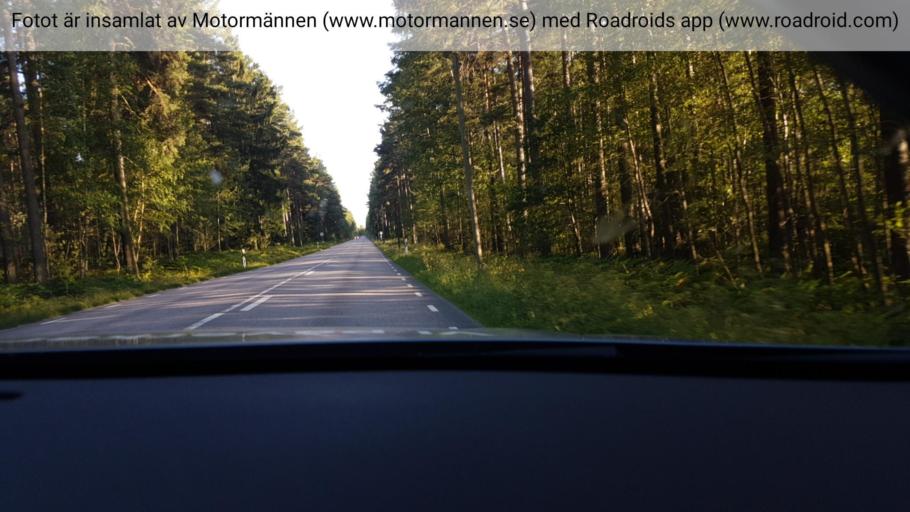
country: SE
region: Vaestra Goetaland
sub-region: Skovde Kommun
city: Stopen
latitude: 58.4649
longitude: 13.9584
